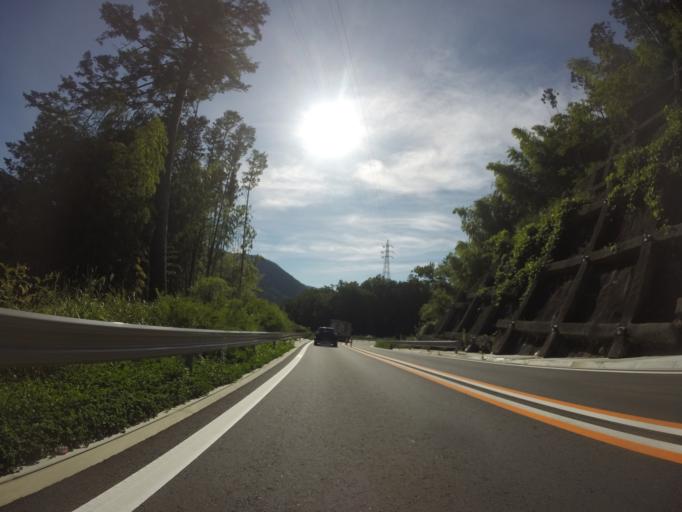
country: JP
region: Shizuoka
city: Fujinomiya
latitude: 35.2515
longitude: 138.4746
